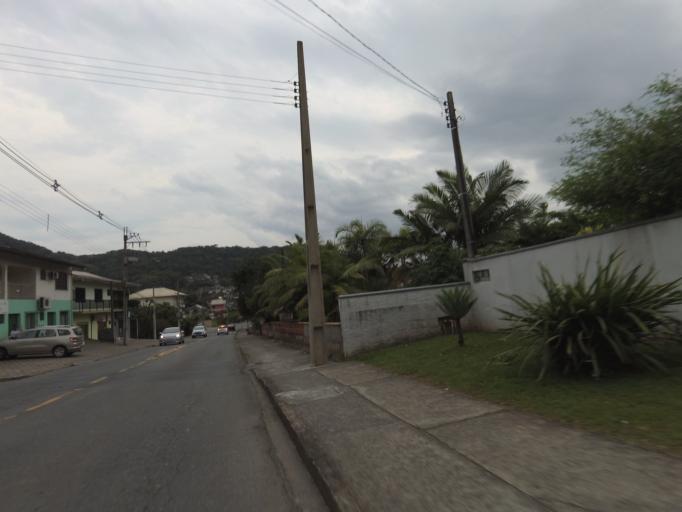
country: BR
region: Santa Catarina
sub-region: Blumenau
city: Blumenau
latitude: -26.8689
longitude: -49.0496
